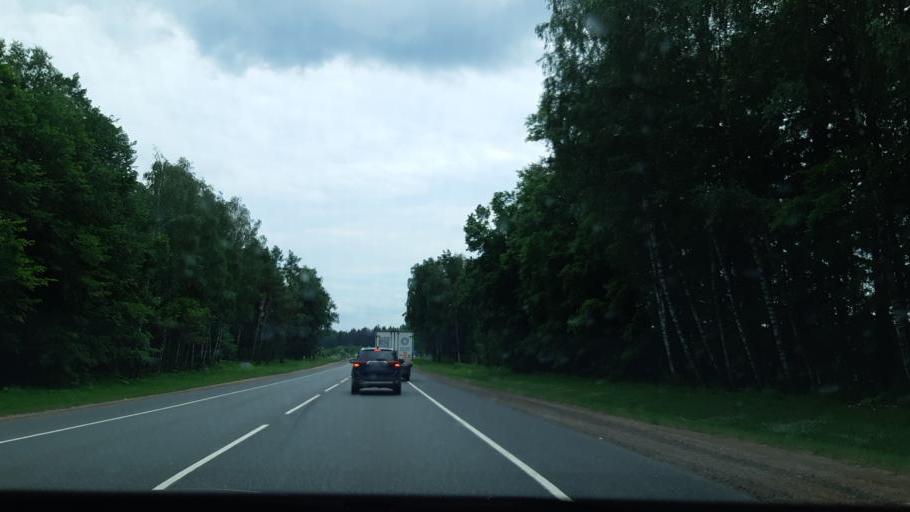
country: RU
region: Moskovskaya
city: Dorokhovo
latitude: 55.4939
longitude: 36.3509
